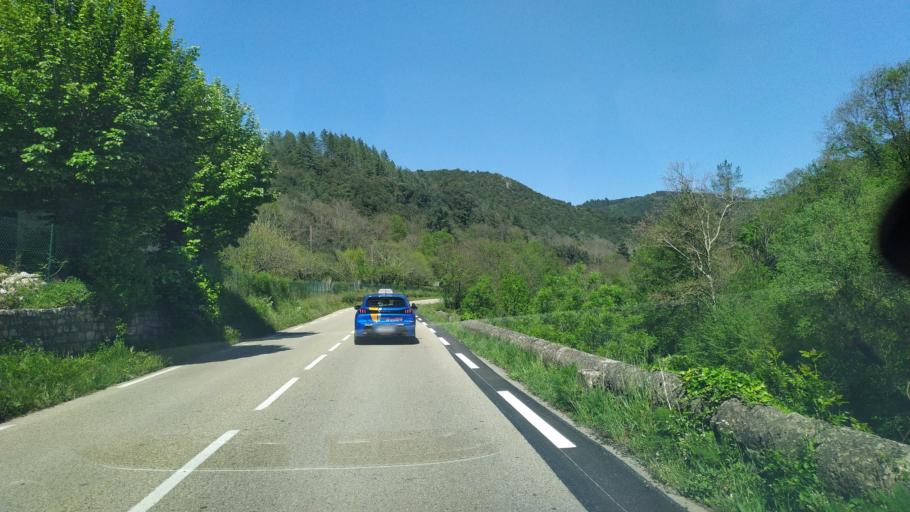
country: FR
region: Languedoc-Roussillon
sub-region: Departement du Gard
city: Le Vigan
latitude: 43.9989
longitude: 3.6480
